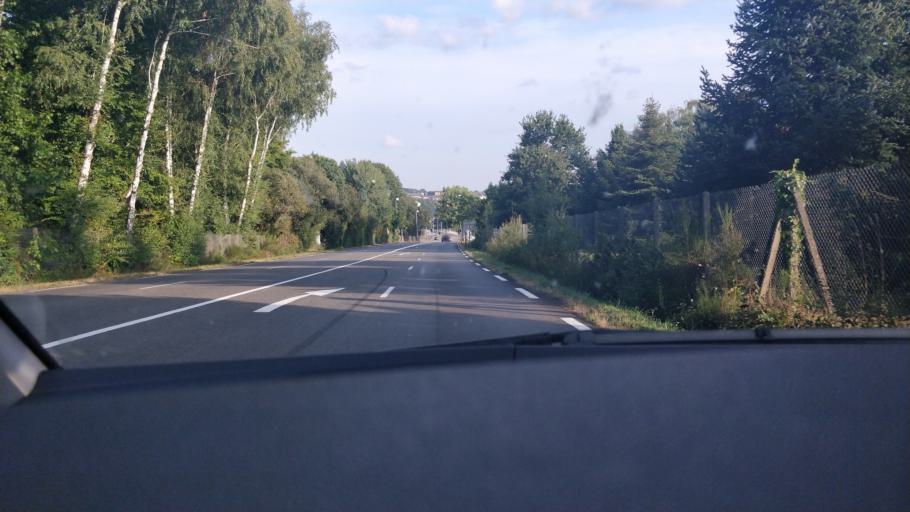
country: FR
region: Limousin
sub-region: Departement de la Haute-Vienne
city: Le Palais-sur-Vienne
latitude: 45.8537
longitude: 1.2955
